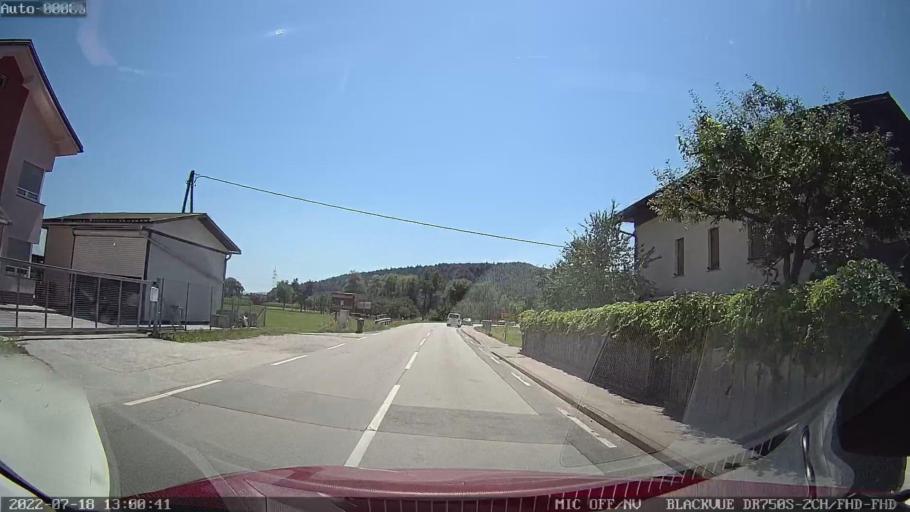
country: SI
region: Dobrova-Horjul-Polhov Gradec
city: Dobrova
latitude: 46.0608
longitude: 14.4134
